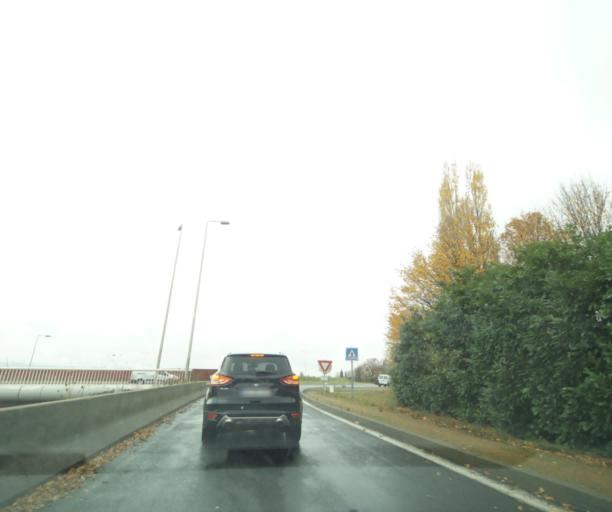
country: FR
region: Auvergne
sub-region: Departement du Puy-de-Dome
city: Perignat-les-Sarlieve
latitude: 45.7443
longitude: 3.1385
